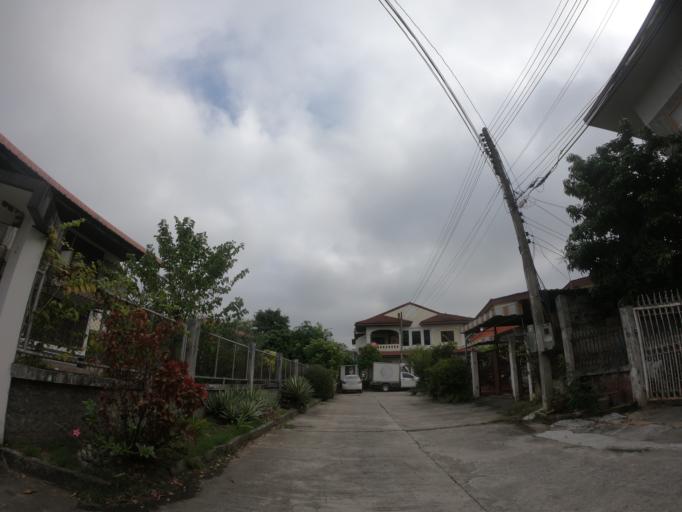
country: TH
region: Chiang Mai
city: Chiang Mai
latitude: 18.7609
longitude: 98.9775
